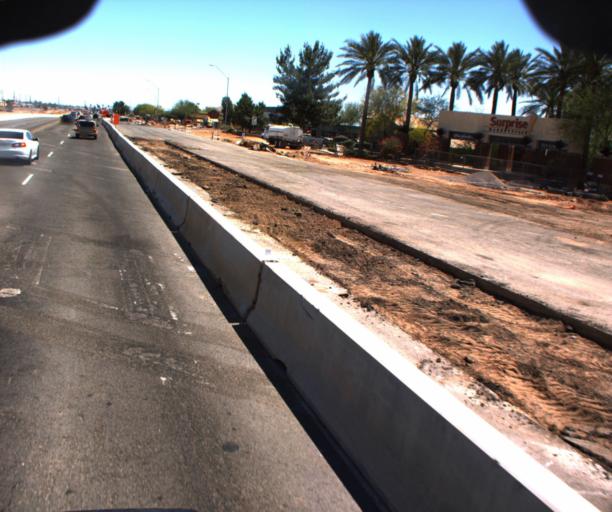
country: US
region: Arizona
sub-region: Maricopa County
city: Surprise
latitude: 33.6389
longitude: -112.3507
